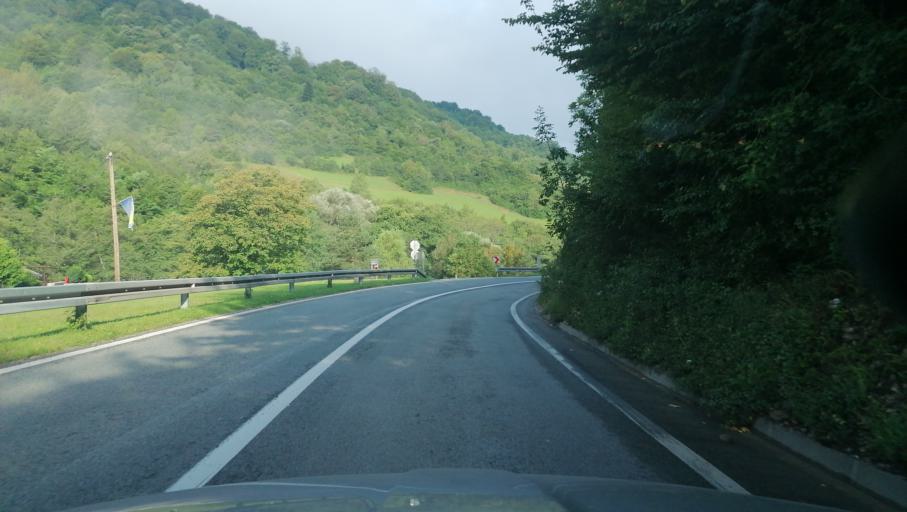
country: BA
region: Federation of Bosnia and Herzegovina
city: Jajce
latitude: 44.2801
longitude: 17.2643
